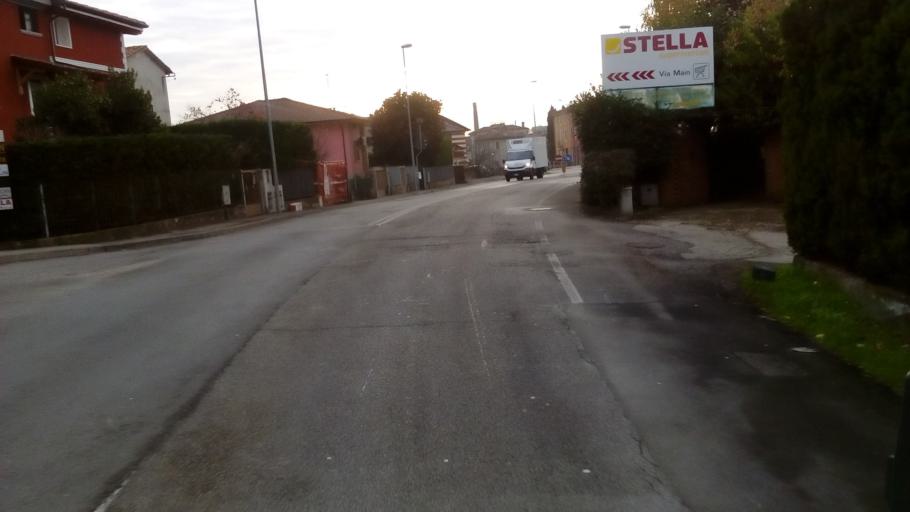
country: IT
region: Veneto
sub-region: Provincia di Vicenza
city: Arzignano
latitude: 45.5252
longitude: 11.3225
